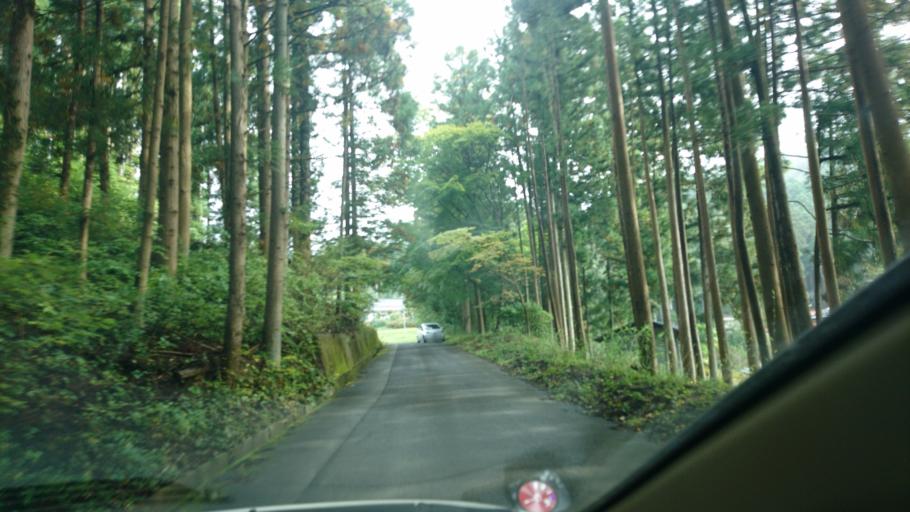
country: JP
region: Iwate
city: Ichinoseki
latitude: 38.9609
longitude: 141.1813
